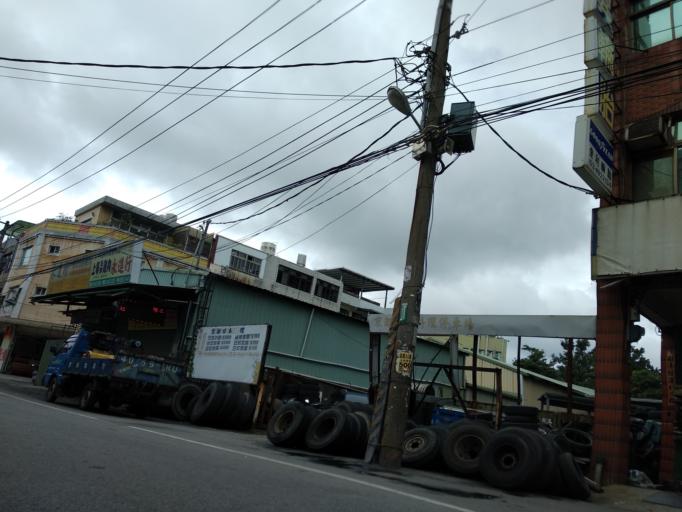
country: TW
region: Taiwan
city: Taoyuan City
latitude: 24.9609
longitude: 121.2088
